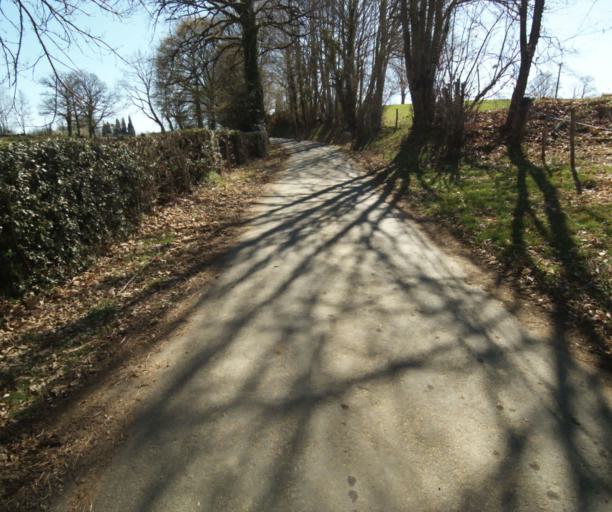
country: FR
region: Limousin
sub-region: Departement de la Correze
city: Seilhac
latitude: 45.3920
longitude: 1.6728
